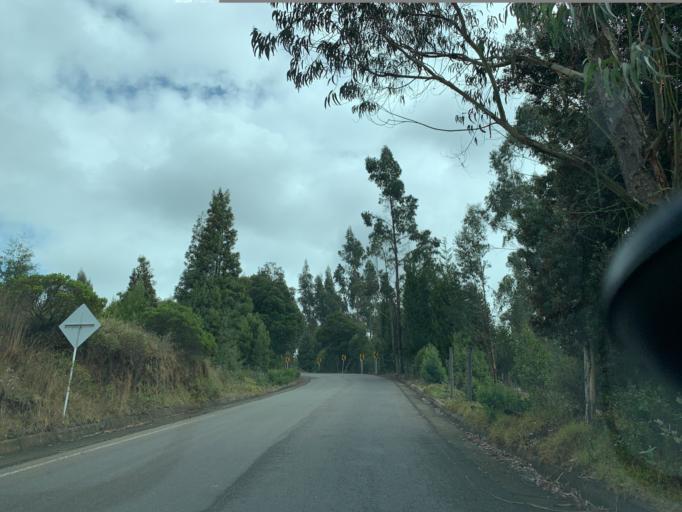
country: CO
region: Boyaca
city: Tunja
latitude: 5.5670
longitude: -73.3625
